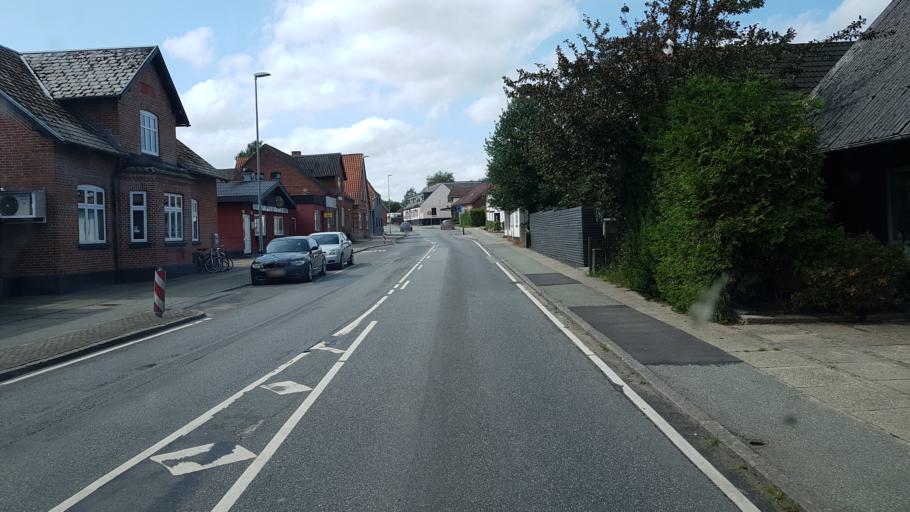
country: DK
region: South Denmark
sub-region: Vejen Kommune
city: Vejen
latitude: 55.5704
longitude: 9.1415
